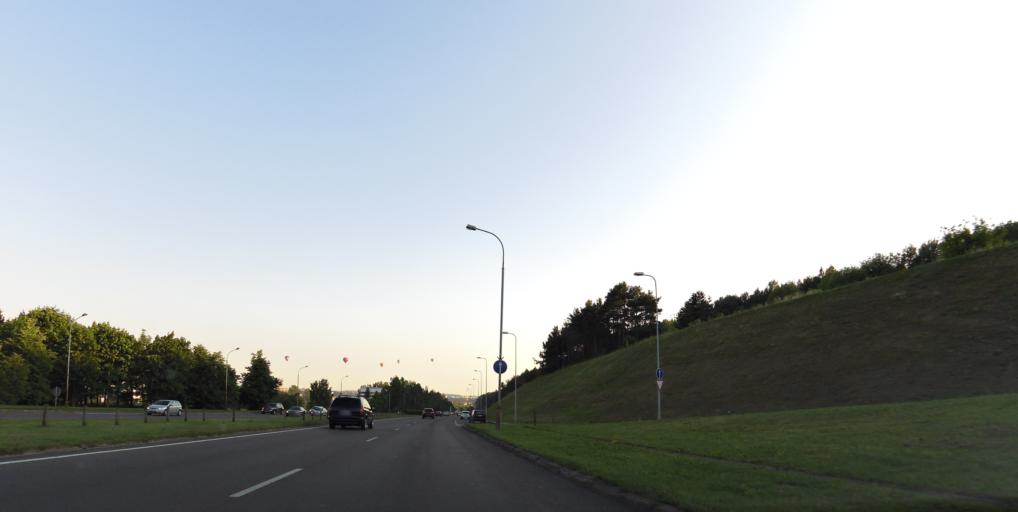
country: LT
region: Vilnius County
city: Seskine
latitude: 54.7119
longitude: 25.2699
